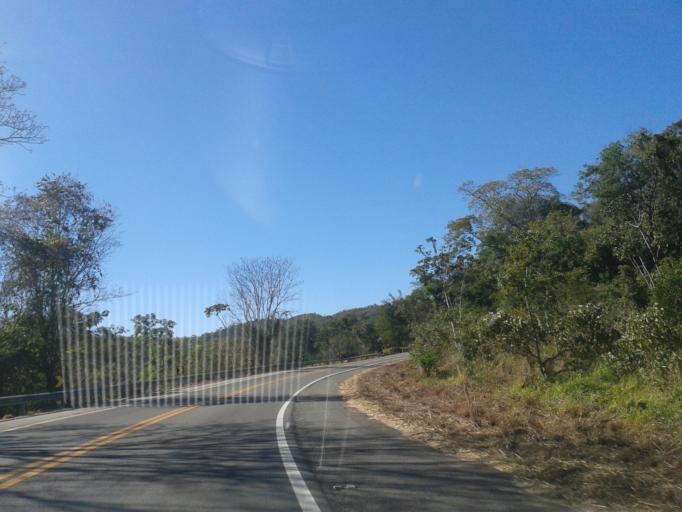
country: BR
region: Goias
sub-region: Goias
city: Goias
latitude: -15.8852
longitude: -50.1062
